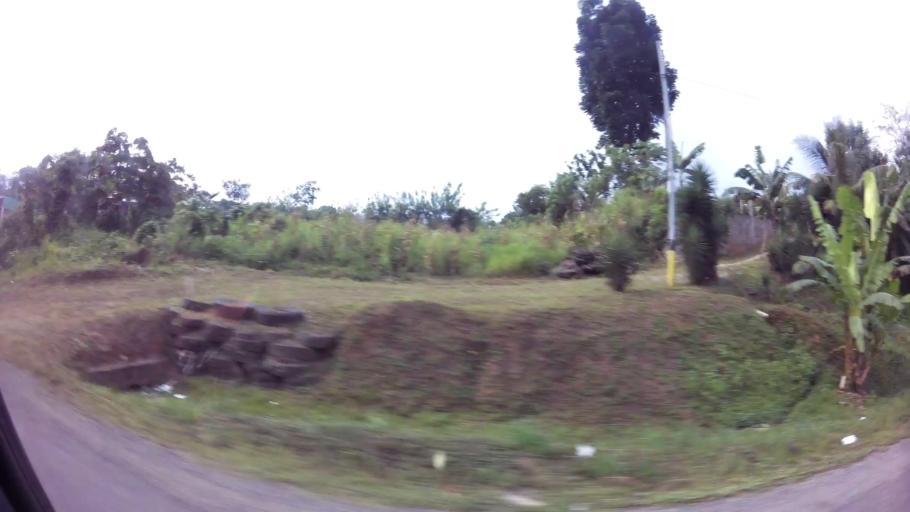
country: HN
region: Yoro
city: Guaimitas
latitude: 15.5113
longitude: -87.6785
